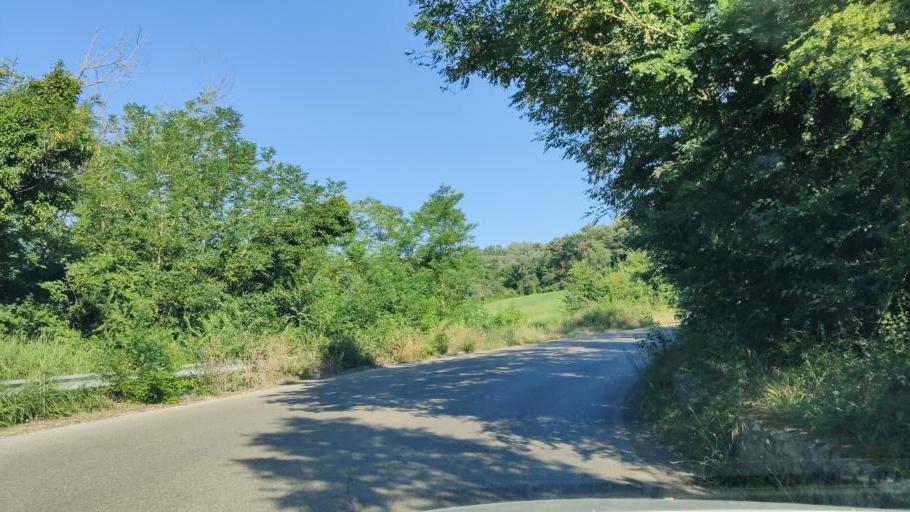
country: IT
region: Umbria
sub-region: Provincia di Terni
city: Penna in Teverina
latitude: 42.4792
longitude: 12.3732
